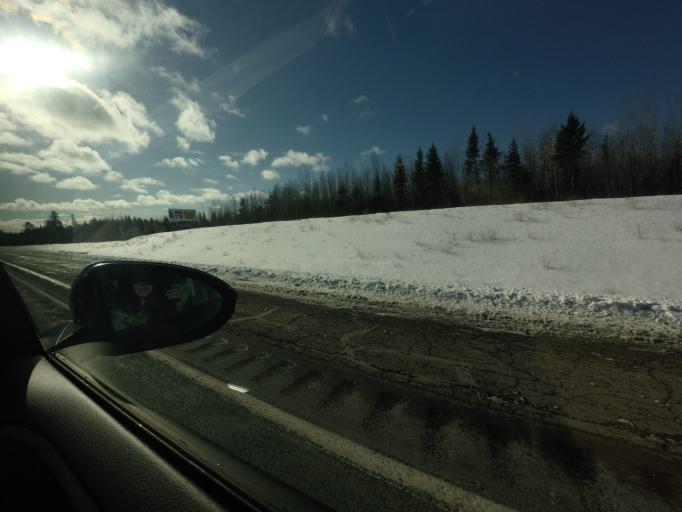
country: CA
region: New Brunswick
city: Fredericton
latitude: 45.8928
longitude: -66.6464
